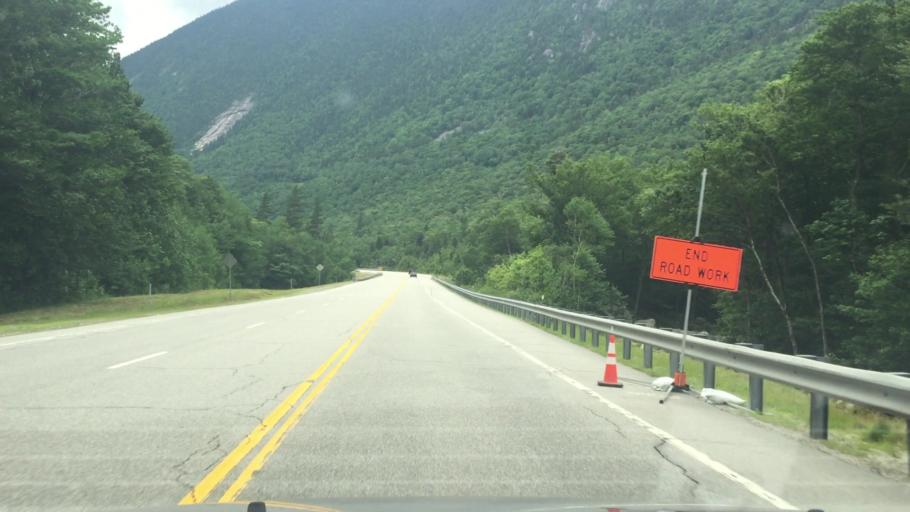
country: US
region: New Hampshire
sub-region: Grafton County
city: Deerfield
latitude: 44.2020
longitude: -71.4053
